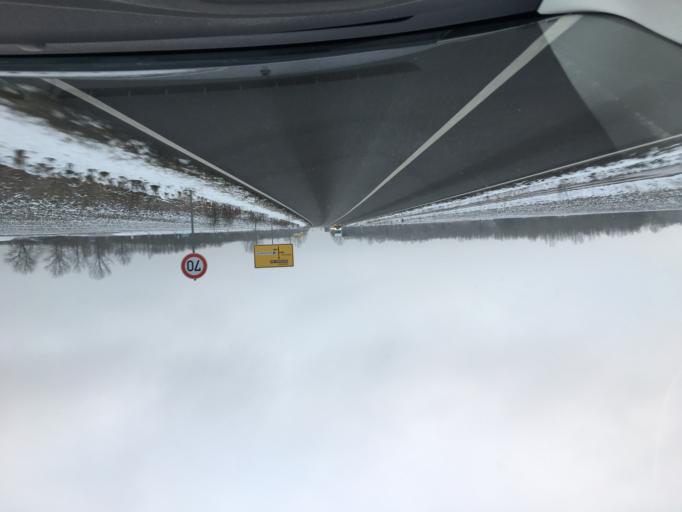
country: DE
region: Saxony
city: Grossposna
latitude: 51.2382
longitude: 12.4878
